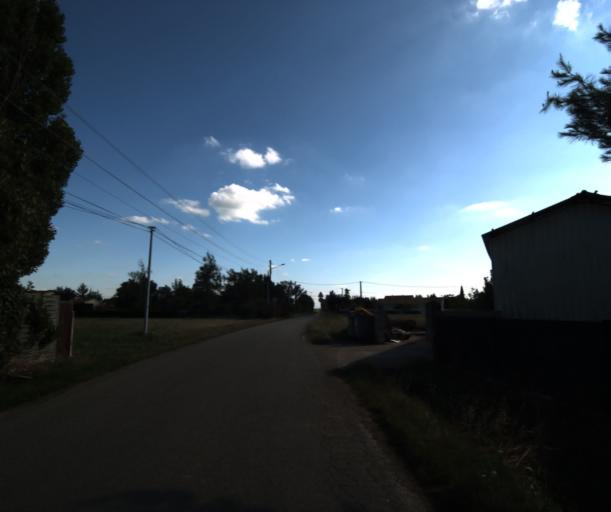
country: FR
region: Midi-Pyrenees
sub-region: Departement de la Haute-Garonne
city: Saint-Lys
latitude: 43.4976
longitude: 1.1918
